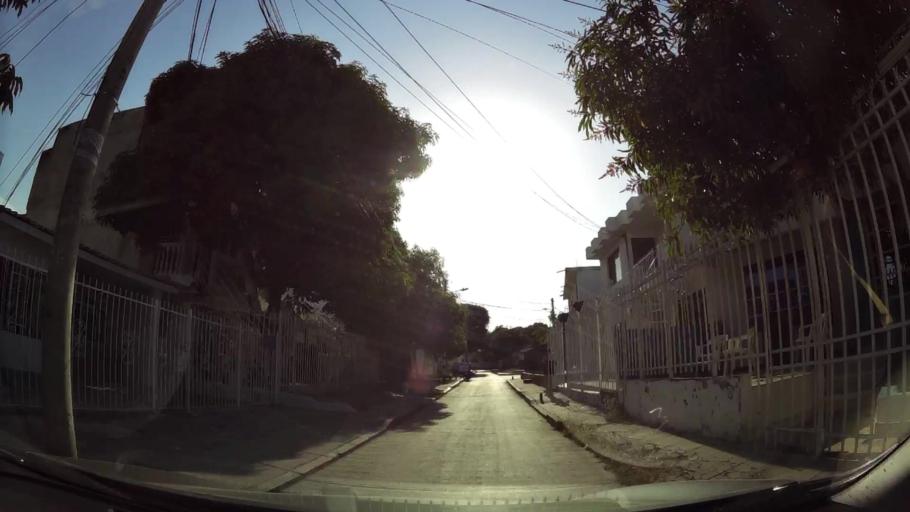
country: CO
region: Bolivar
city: Cartagena
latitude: 10.3871
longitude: -75.4830
